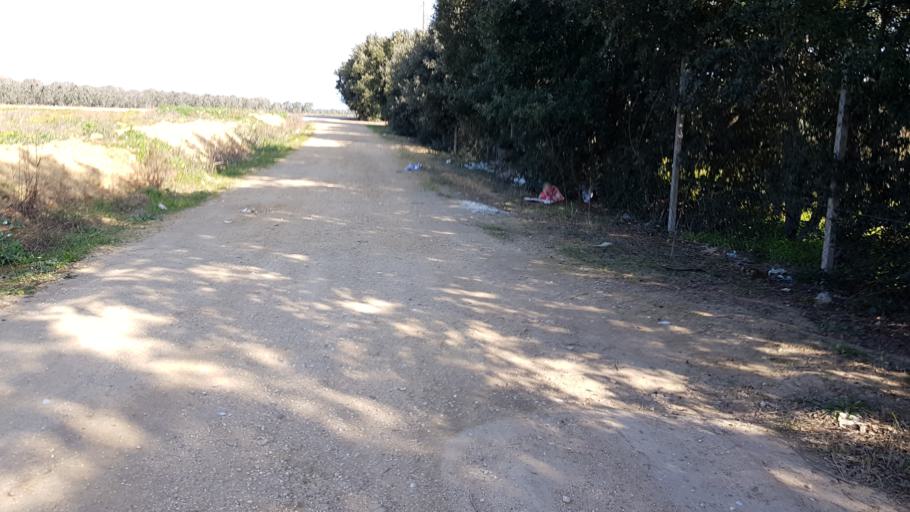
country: IT
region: Apulia
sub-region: Provincia di Brindisi
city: Mesagne
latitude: 40.5878
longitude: 17.8618
